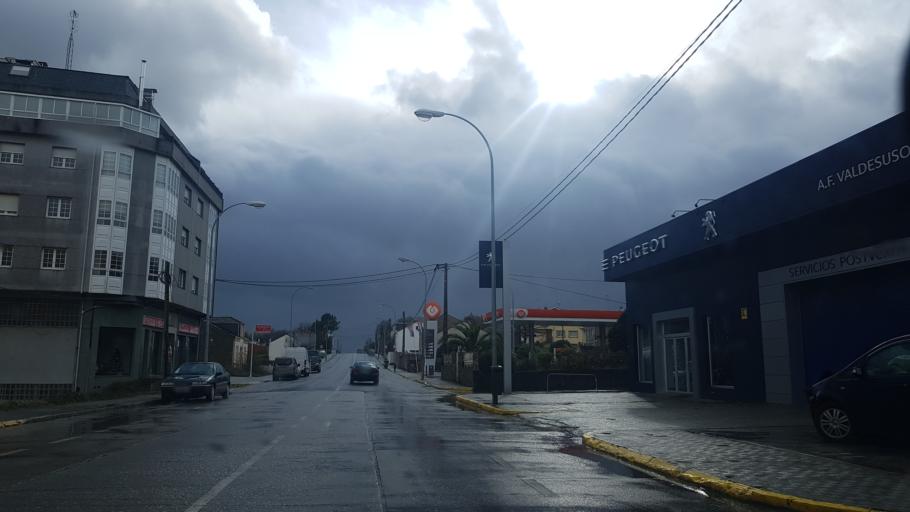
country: ES
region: Galicia
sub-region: Provincia de Lugo
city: Vilalba
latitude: 43.2896
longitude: -7.6791
